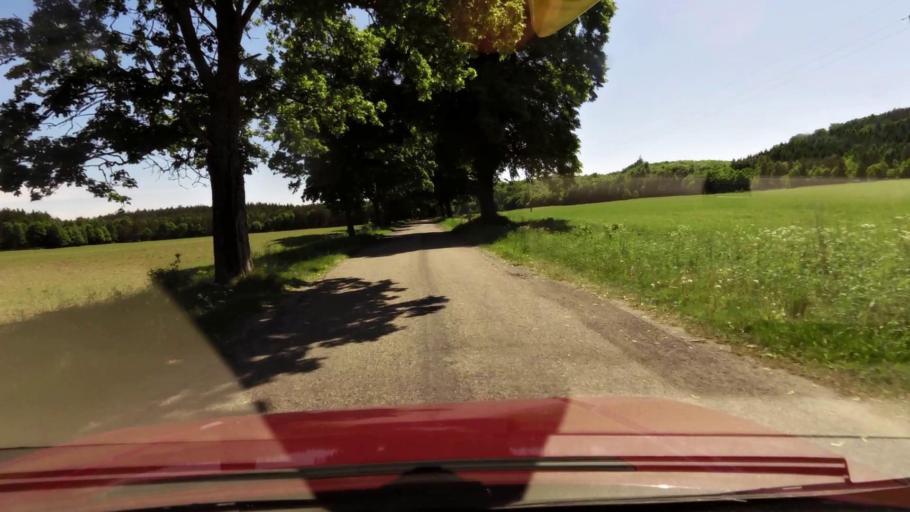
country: PL
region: West Pomeranian Voivodeship
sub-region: Powiat koszalinski
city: Bobolice
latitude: 54.0358
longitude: 16.6095
